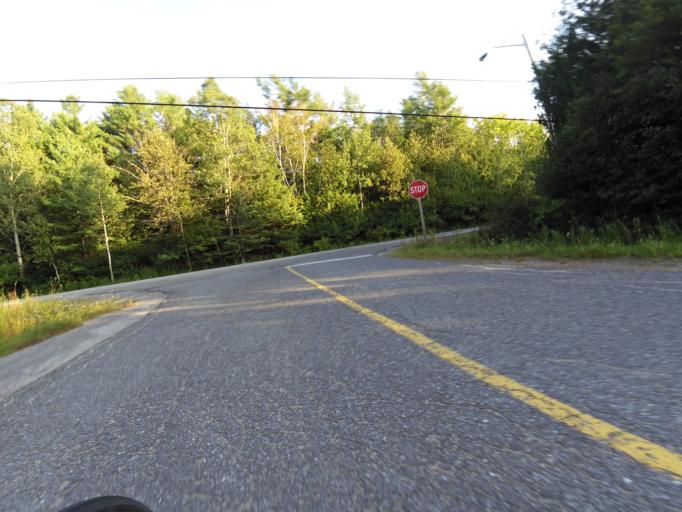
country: CA
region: Ontario
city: Bells Corners
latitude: 45.3787
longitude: -75.9544
